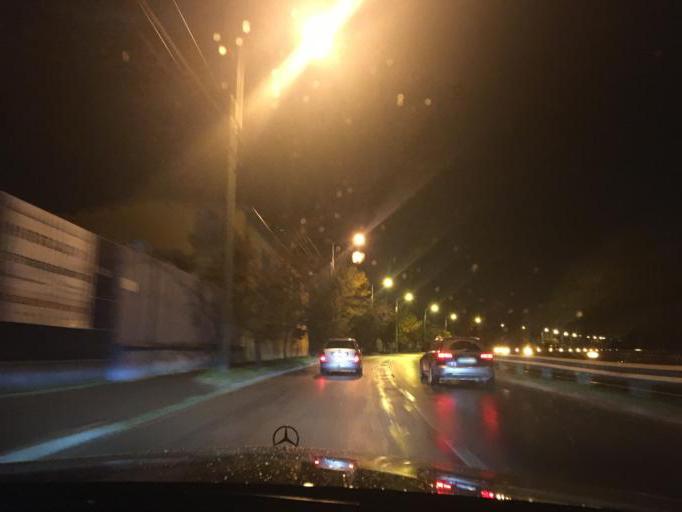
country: RO
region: Bihor
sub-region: Comuna Biharea
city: Oradea
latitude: 47.0504
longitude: 21.9555
